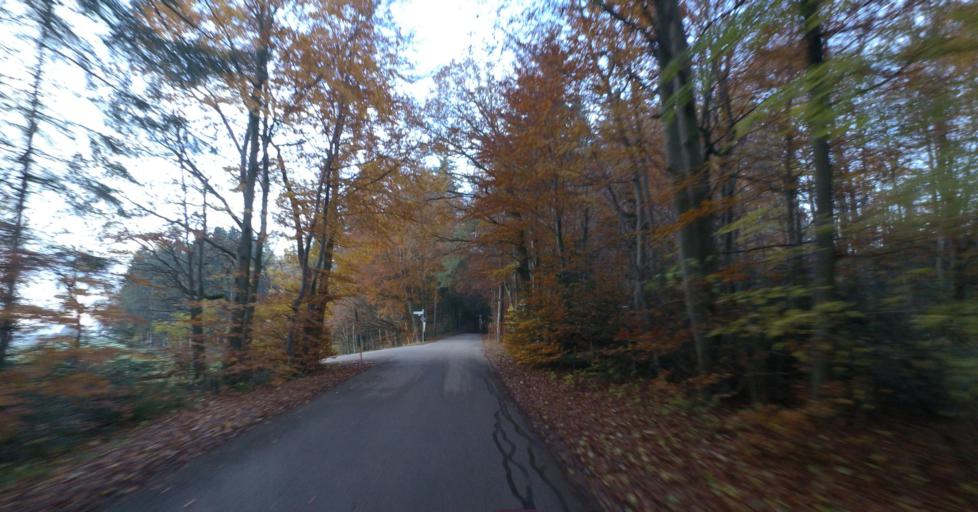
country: DE
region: Bavaria
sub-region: Upper Bavaria
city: Nussdorf
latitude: 47.8905
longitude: 12.6022
